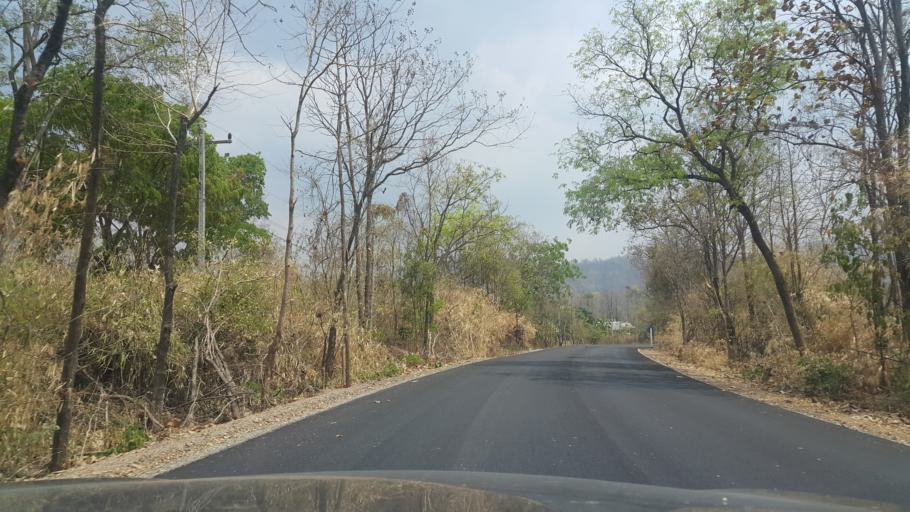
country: TH
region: Lamphun
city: Ban Hong
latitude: 18.2475
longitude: 98.9585
